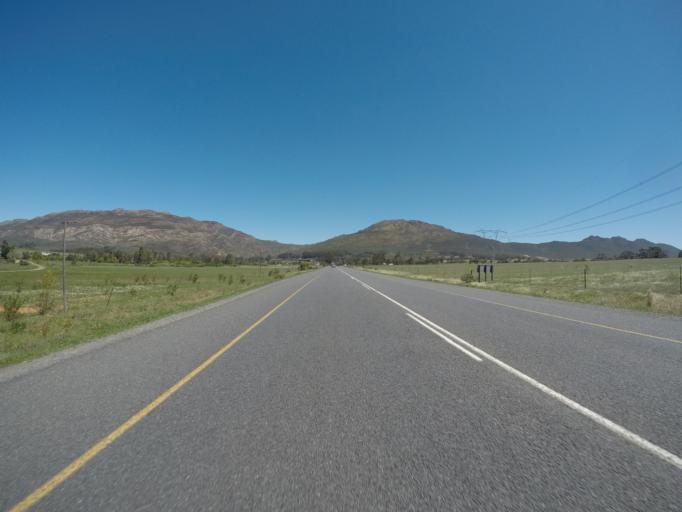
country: ZA
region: Western Cape
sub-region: Cape Winelands District Municipality
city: Ceres
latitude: -33.3083
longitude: 19.1093
